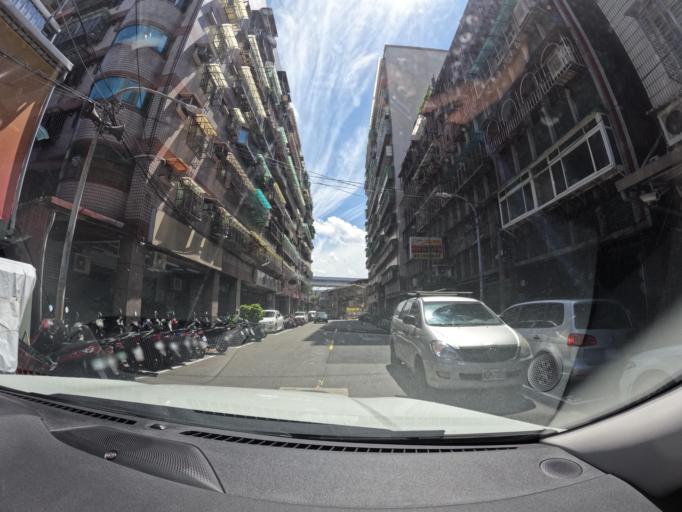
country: TW
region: Taipei
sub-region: Taipei
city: Banqiao
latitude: 25.0235
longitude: 121.4827
